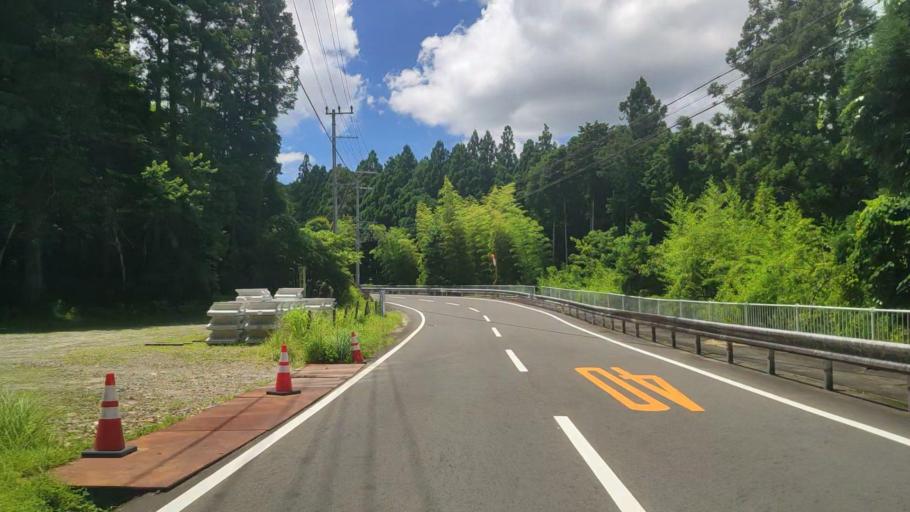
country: JP
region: Mie
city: Owase
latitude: 33.9528
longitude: 136.0690
